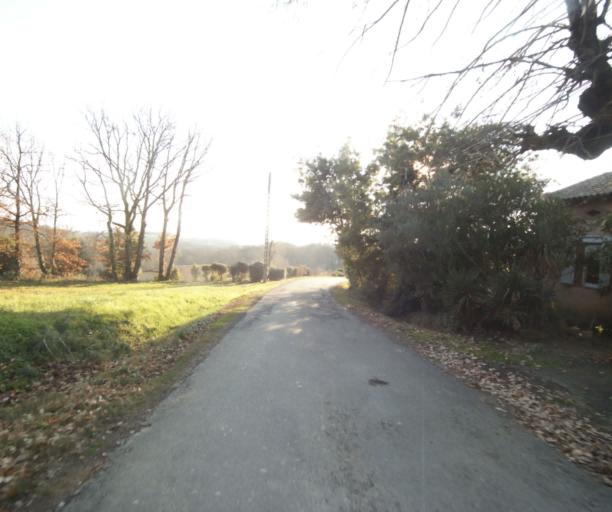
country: FR
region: Midi-Pyrenees
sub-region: Departement du Tarn-et-Garonne
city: Moissac
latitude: 44.1405
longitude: 1.1395
